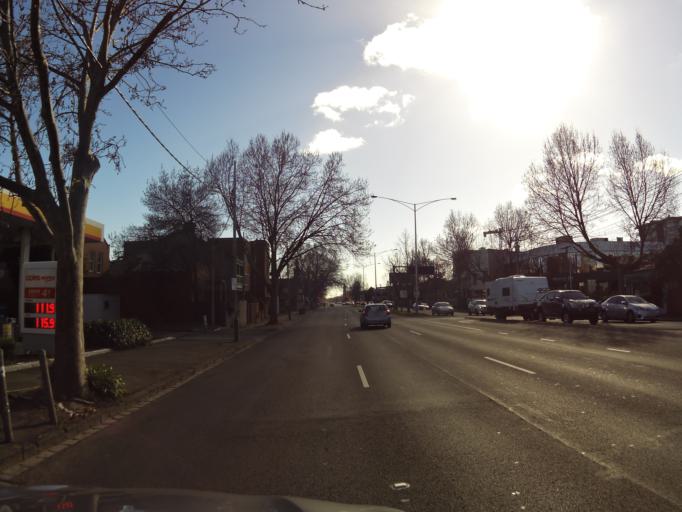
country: AU
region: Victoria
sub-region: Melbourne
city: East Melbourne
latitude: -37.8133
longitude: 144.9906
